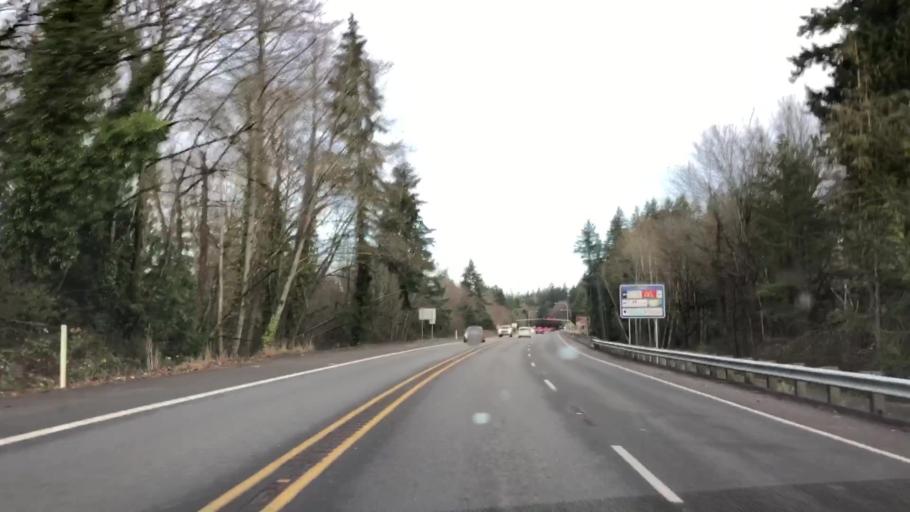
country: US
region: Washington
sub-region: Kitsap County
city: Bainbridge Island
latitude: 47.6317
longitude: -122.5160
